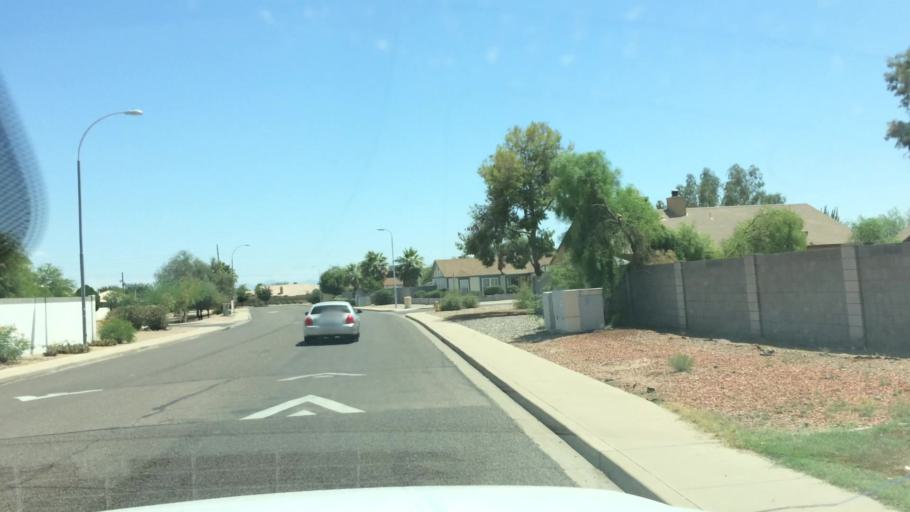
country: US
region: Arizona
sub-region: Maricopa County
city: Peoria
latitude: 33.5974
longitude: -112.2415
